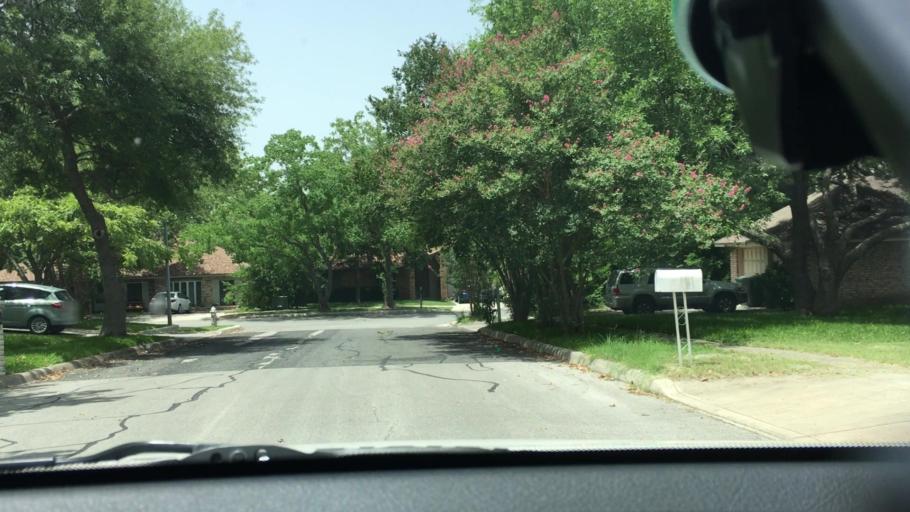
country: US
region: Texas
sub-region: Bexar County
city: Live Oak
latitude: 29.5758
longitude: -98.3648
